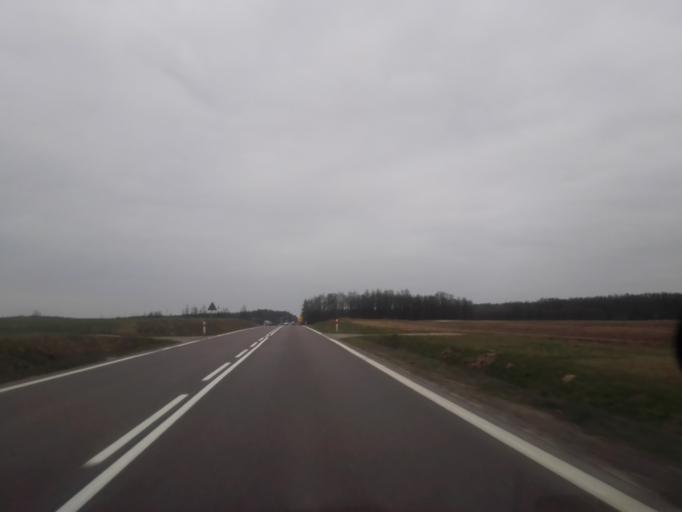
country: PL
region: Podlasie
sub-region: Powiat grajewski
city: Szczuczyn
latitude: 53.5314
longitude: 22.2589
